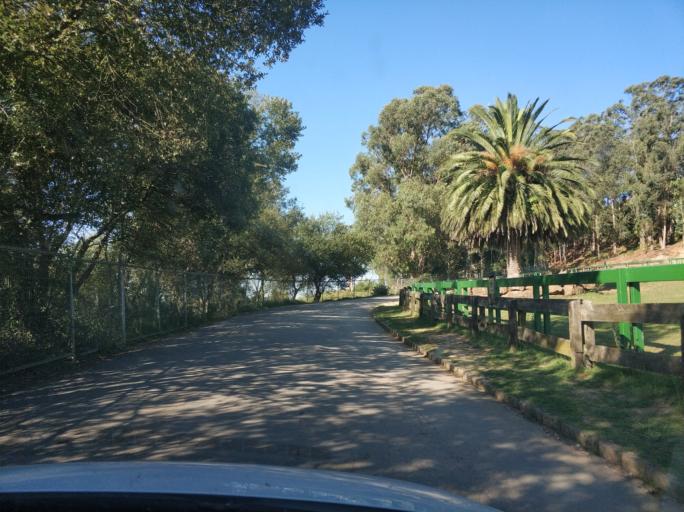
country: ES
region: Cantabria
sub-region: Provincia de Cantabria
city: Penagos
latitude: 43.3469
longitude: -3.8446
